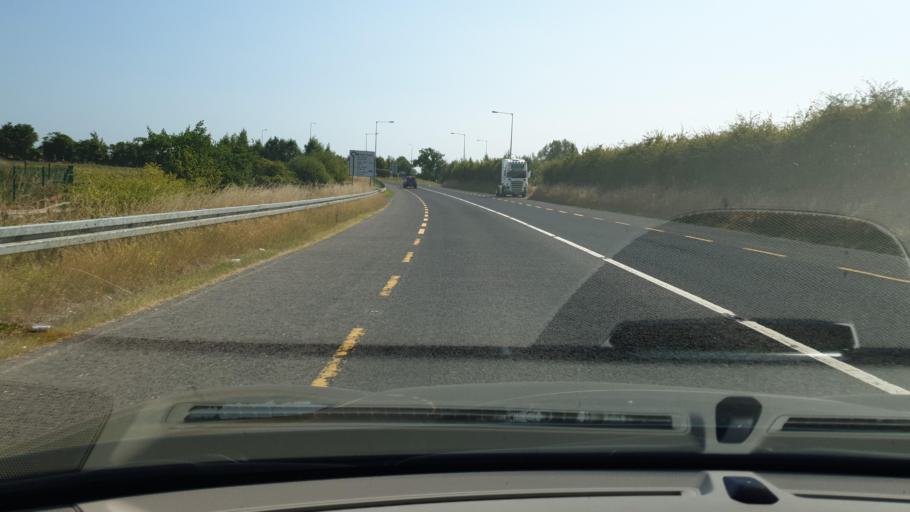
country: IE
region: Leinster
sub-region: An Mhi
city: Dunshaughlin
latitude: 53.5116
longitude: -6.5573
